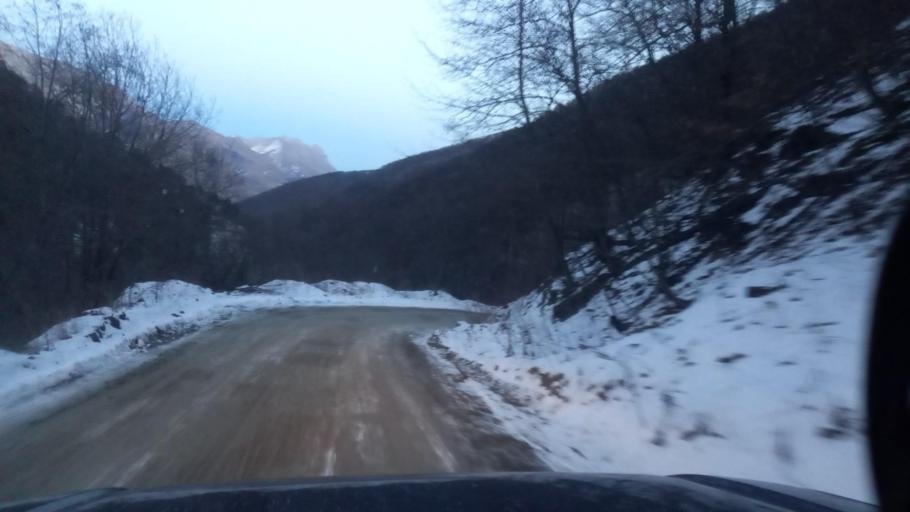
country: RU
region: Ingushetiya
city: Dzhayrakh
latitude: 42.8250
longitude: 44.5925
